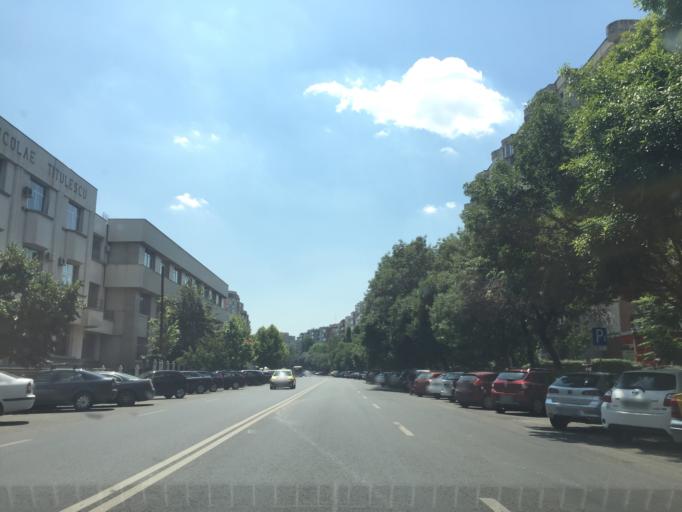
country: RO
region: Bucuresti
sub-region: Municipiul Bucuresti
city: Bucharest
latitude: 44.4145
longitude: 26.1137
